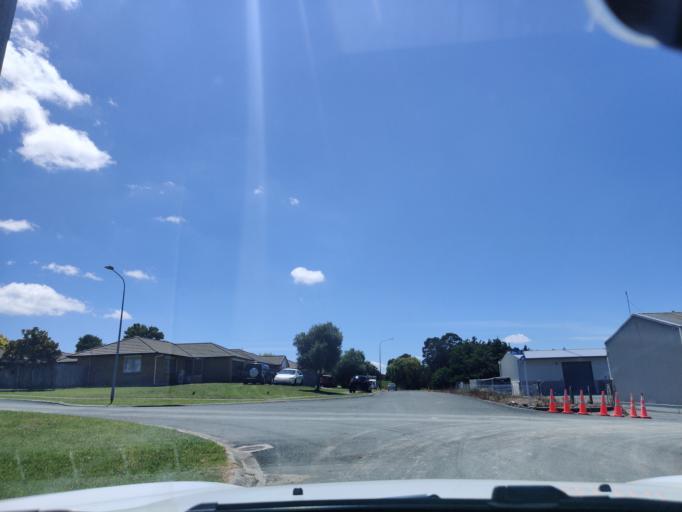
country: NZ
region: Waikato
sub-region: Waikato District
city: Te Kauwhata
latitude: -37.4054
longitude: 175.1527
